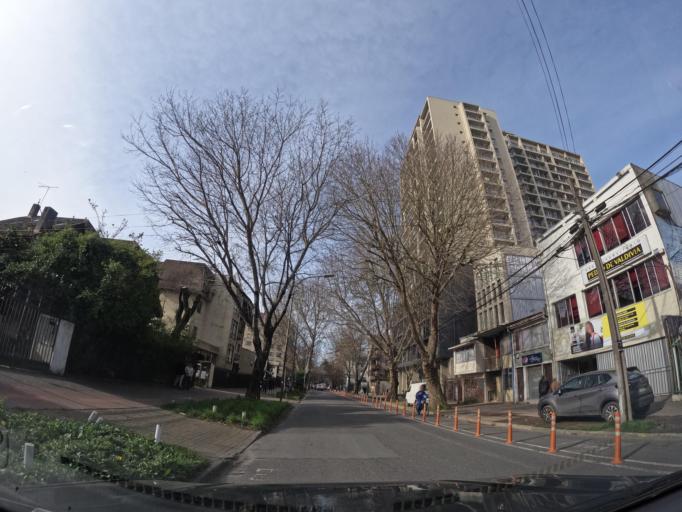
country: CL
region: Biobio
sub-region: Provincia de Concepcion
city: Concepcion
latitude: -36.8215
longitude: -73.0383
